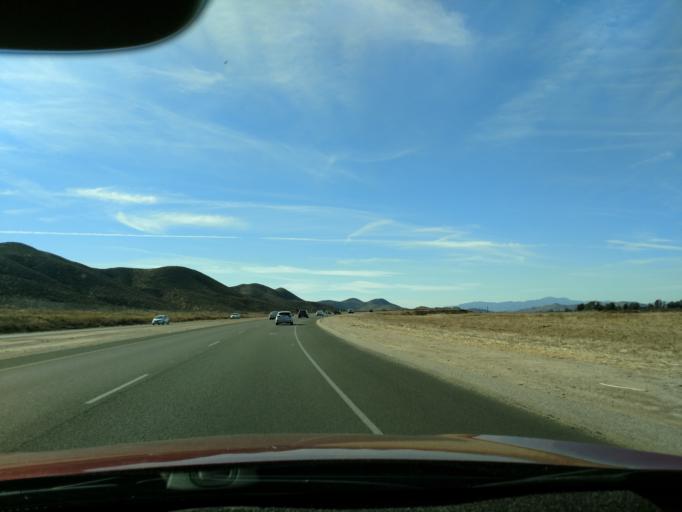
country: US
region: California
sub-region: Riverside County
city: Winchester
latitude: 33.6995
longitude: -117.0401
